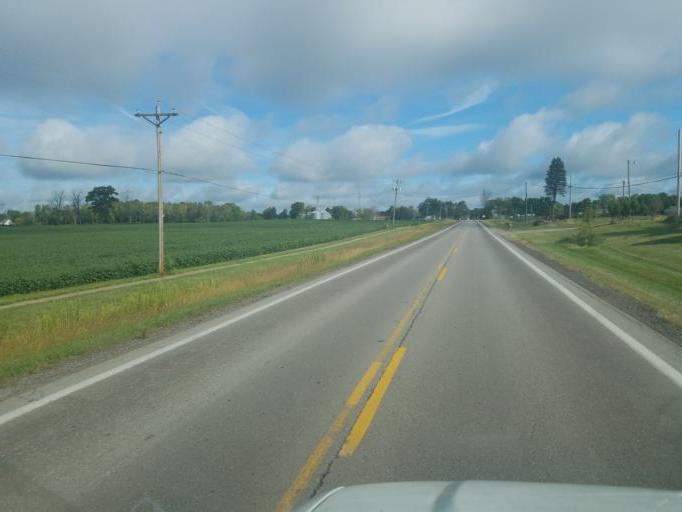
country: US
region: Ohio
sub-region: Wayne County
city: West Salem
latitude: 40.9628
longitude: -82.1096
